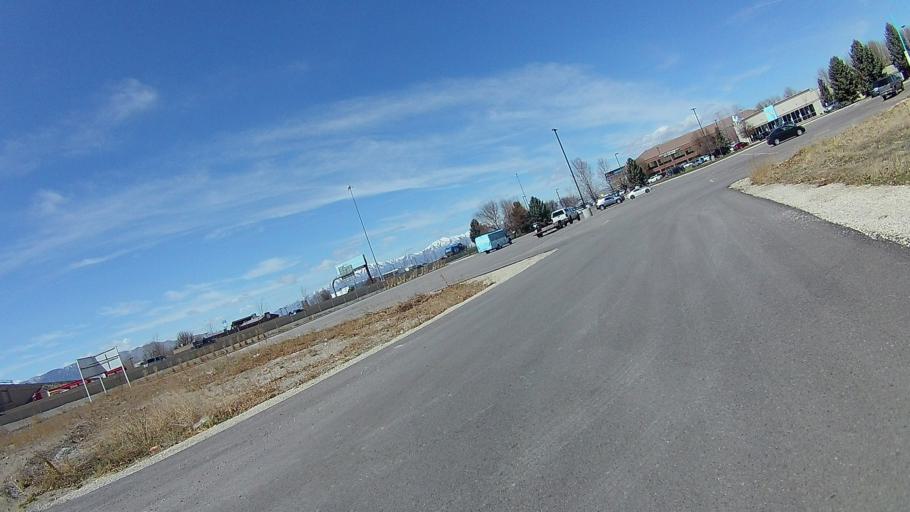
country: US
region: Utah
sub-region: Utah County
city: American Fork
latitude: 40.3563
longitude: -111.7771
